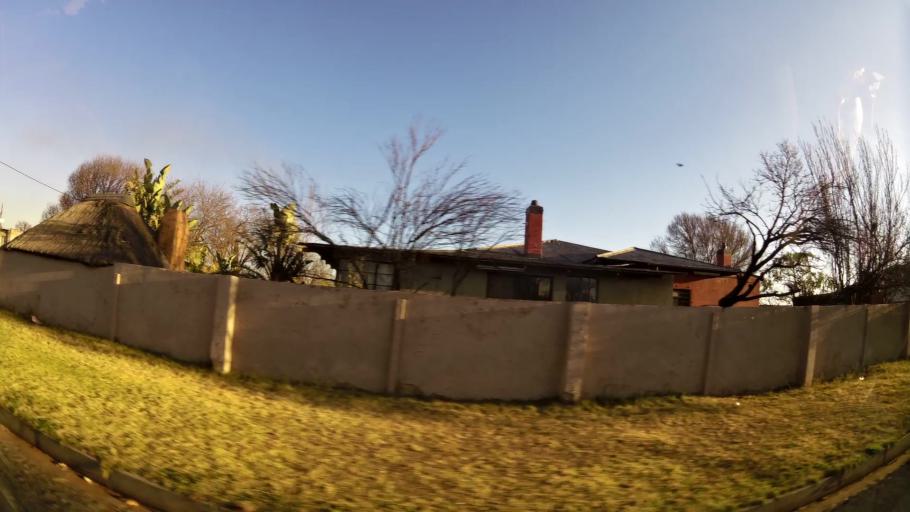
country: ZA
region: Gauteng
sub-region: City of Johannesburg Metropolitan Municipality
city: Roodepoort
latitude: -26.1758
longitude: 27.9429
